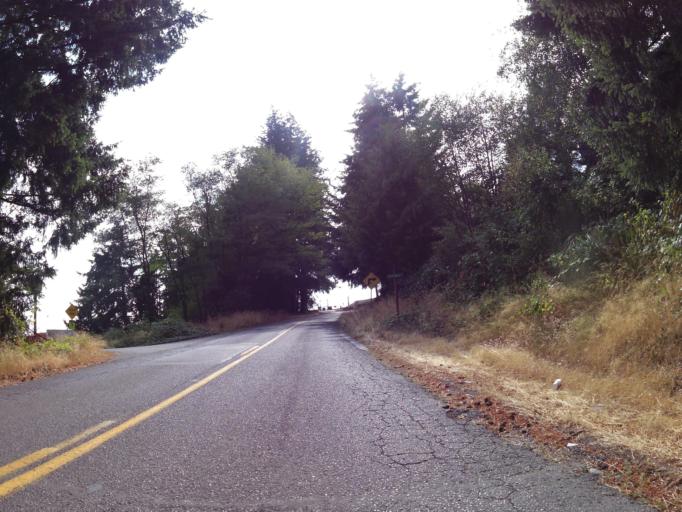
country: US
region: Washington
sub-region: Kitsap County
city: Navy Yard City
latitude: 47.5512
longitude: -122.6755
